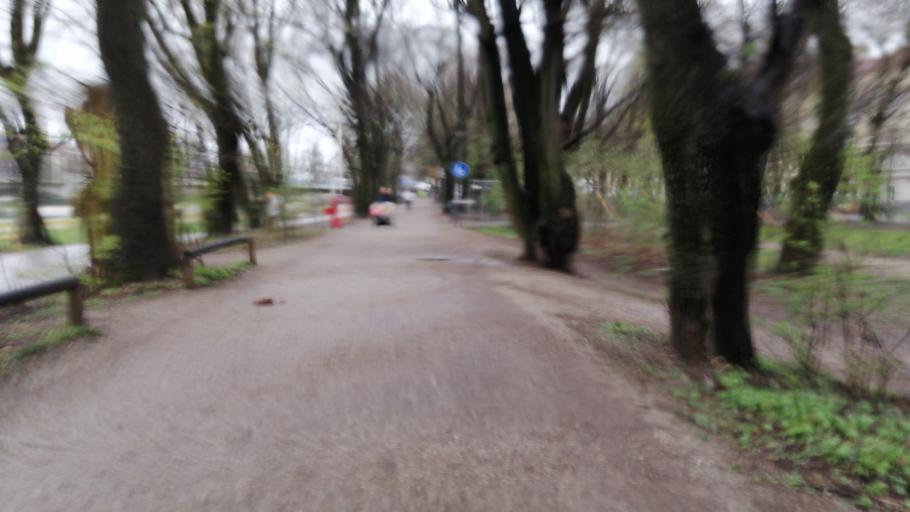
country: DE
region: Bavaria
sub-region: Upper Bavaria
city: Munich
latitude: 48.1256
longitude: 11.5759
